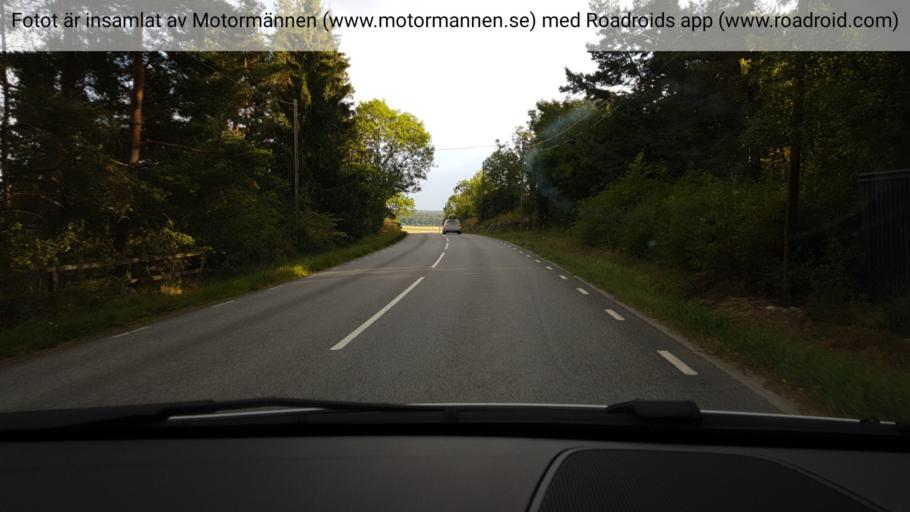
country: SE
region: Stockholm
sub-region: Sigtuna Kommun
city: Sigtuna
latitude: 59.6801
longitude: 17.6981
